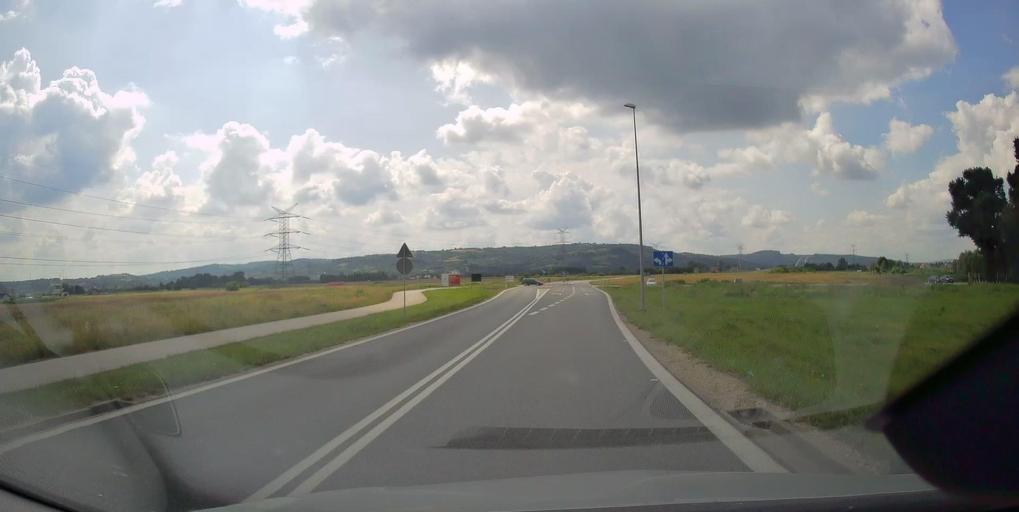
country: PL
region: Lesser Poland Voivodeship
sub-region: Powiat tarnowski
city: Wojnicz
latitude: 49.9605
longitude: 20.8511
